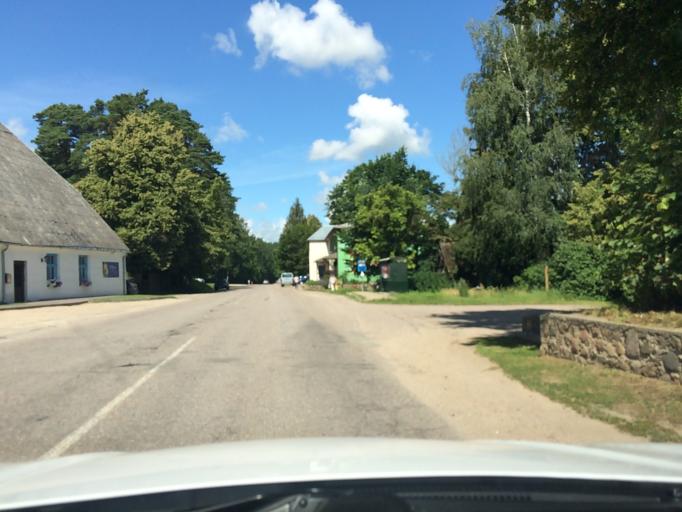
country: LV
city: Tervete
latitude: 56.4800
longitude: 23.3815
